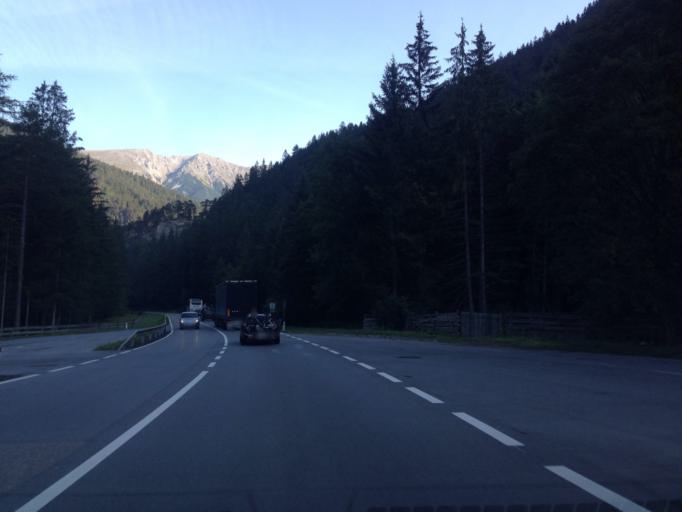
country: AT
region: Tyrol
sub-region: Politischer Bezirk Imst
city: Nassereith
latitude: 47.3349
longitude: 10.8189
